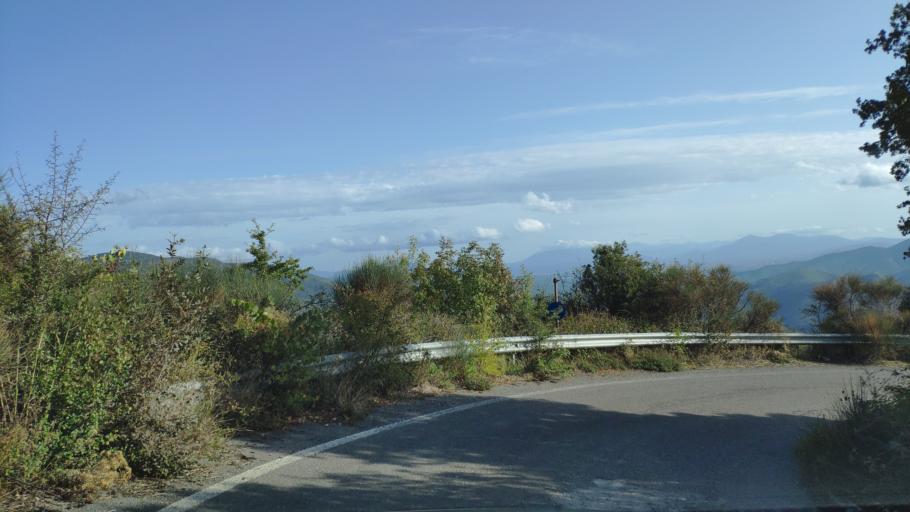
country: GR
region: Peloponnese
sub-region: Nomos Arkadias
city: Dimitsana
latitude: 37.5616
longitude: 22.0321
